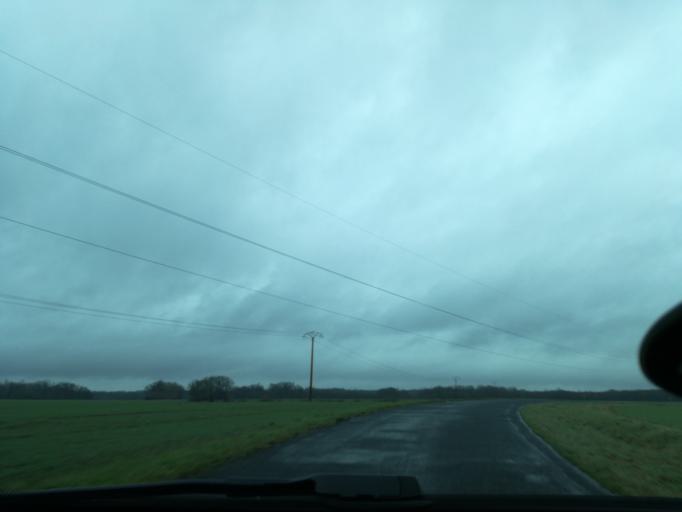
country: FR
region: Lorraine
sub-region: Departement de la Meuse
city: Revigny-sur-Ornain
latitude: 48.8451
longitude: 5.0495
